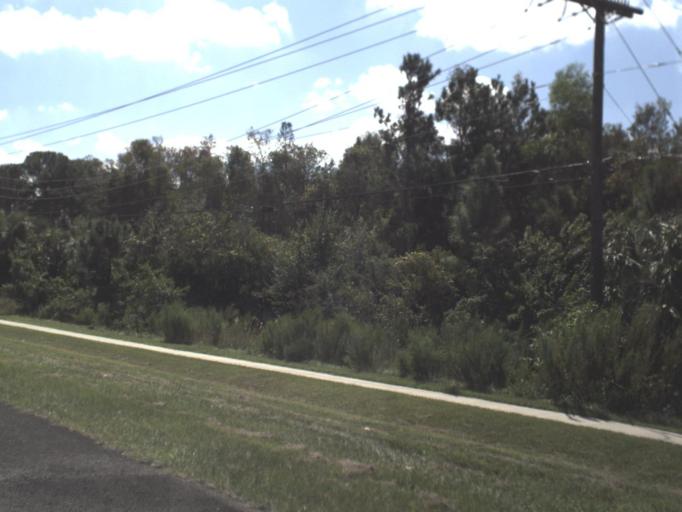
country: US
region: Florida
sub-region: Lee County
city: Estero
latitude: 26.4476
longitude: -81.8173
